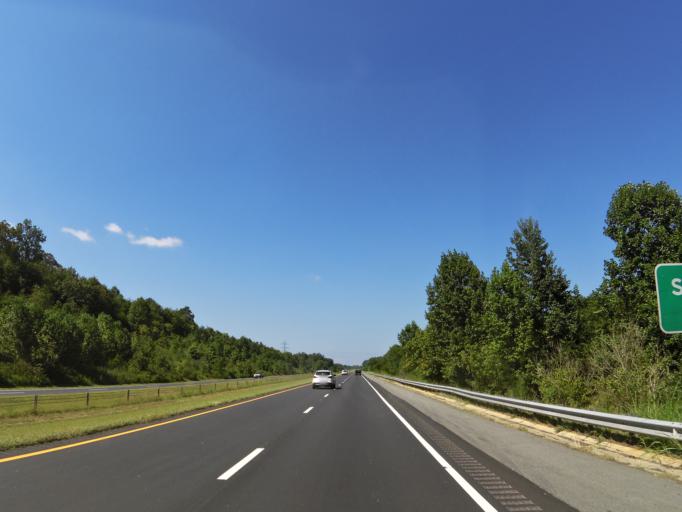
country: US
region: North Carolina
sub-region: Catawba County
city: Maiden
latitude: 35.5628
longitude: -81.2478
